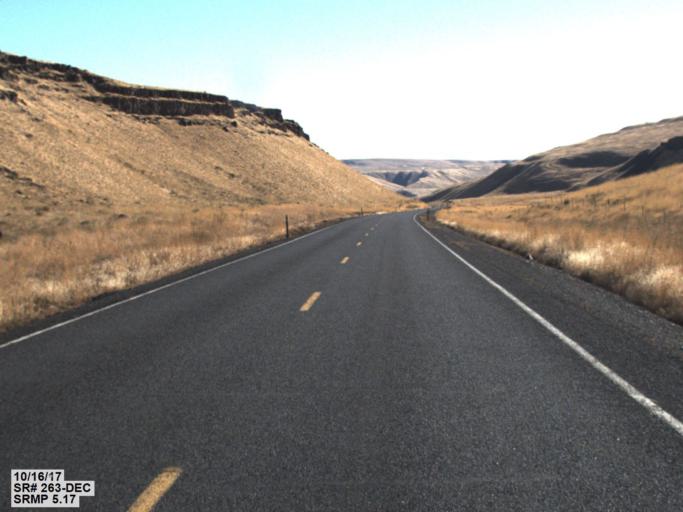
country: US
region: Washington
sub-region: Franklin County
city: Connell
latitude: 46.5901
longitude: -118.5446
